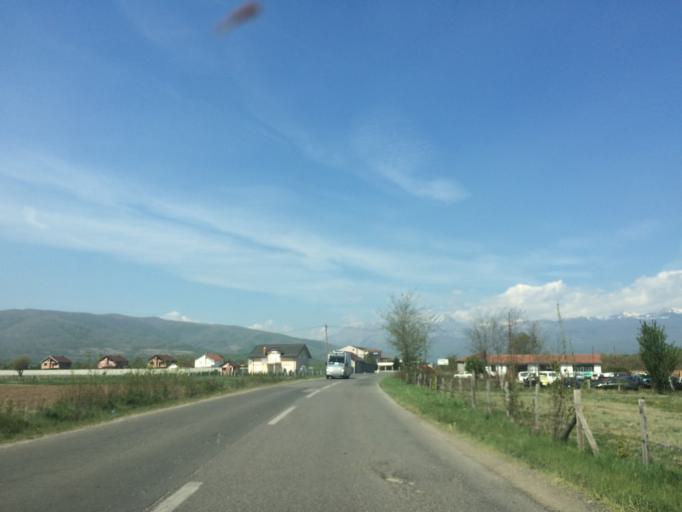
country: XK
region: Gjakova
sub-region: Komuna e Gjakoves
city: Gjakove
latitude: 42.3723
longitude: 20.3494
